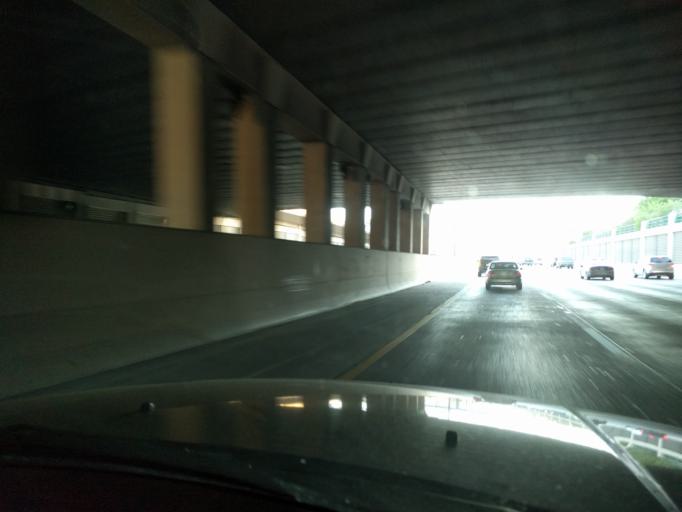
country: US
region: Texas
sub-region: Dallas County
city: Highland Park
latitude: 32.8221
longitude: -96.7861
